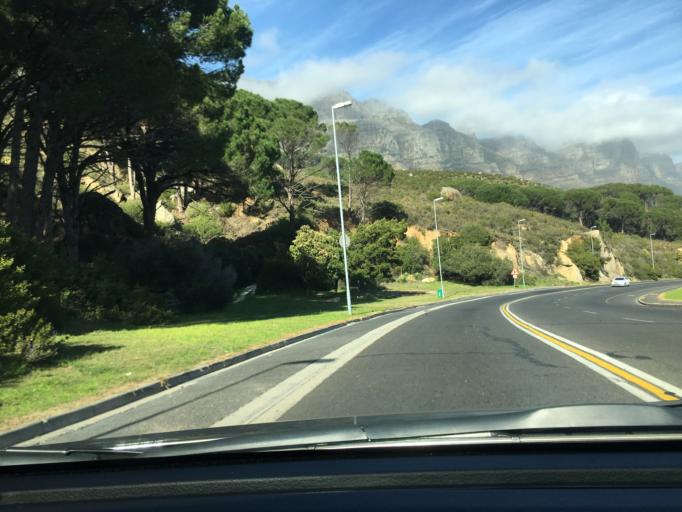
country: ZA
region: Western Cape
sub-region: City of Cape Town
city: Cape Town
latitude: -33.9457
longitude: 18.3924
